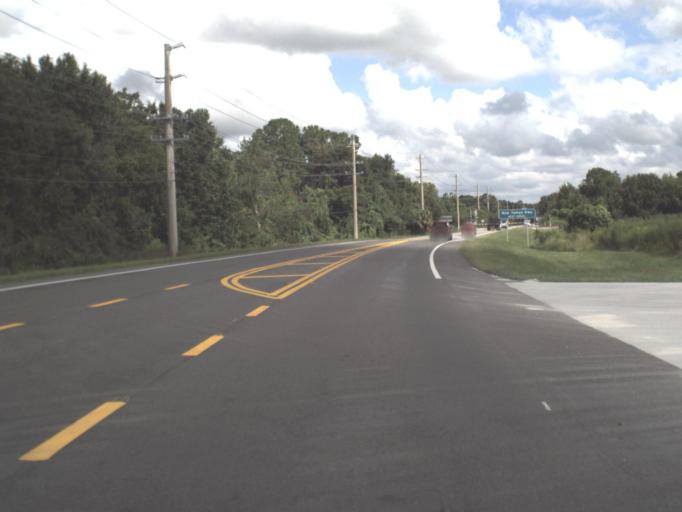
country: US
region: Florida
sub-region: Polk County
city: Winston
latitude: 28.0309
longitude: -82.0189
